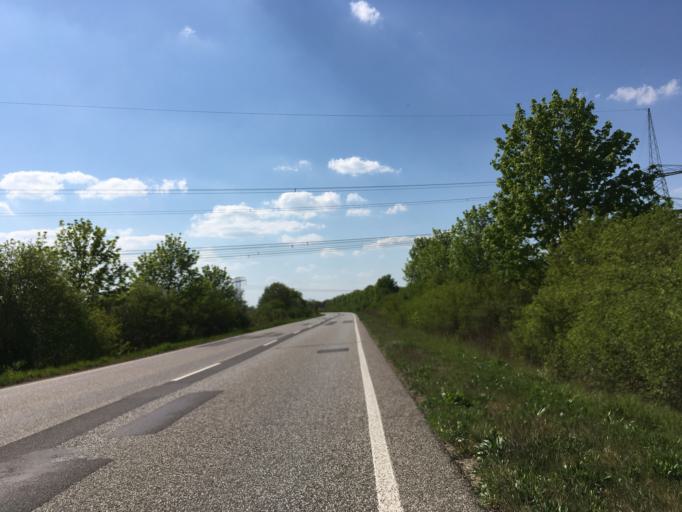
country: DE
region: Brandenburg
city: Werneuchen
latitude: 52.6113
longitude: 13.6629
